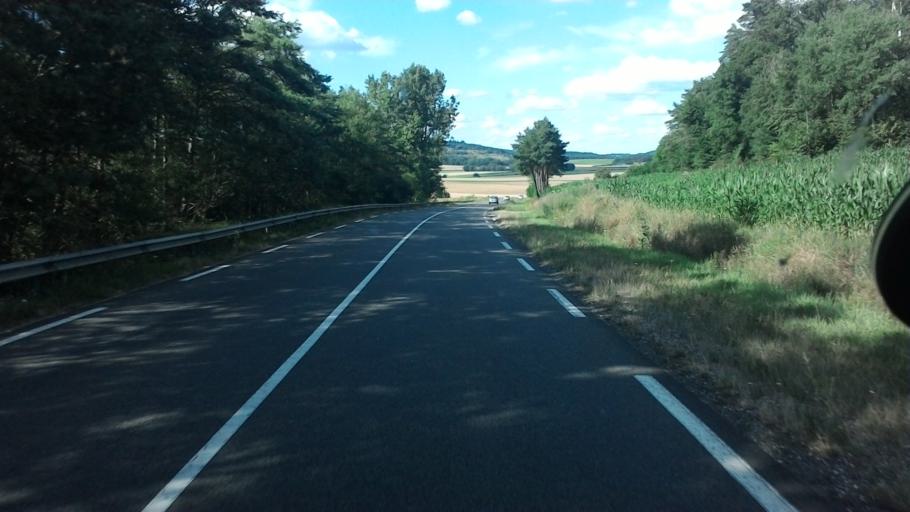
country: FR
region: Franche-Comte
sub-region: Departement de la Haute-Saone
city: Noidans-les-Vesoul
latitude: 47.5557
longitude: 6.0659
